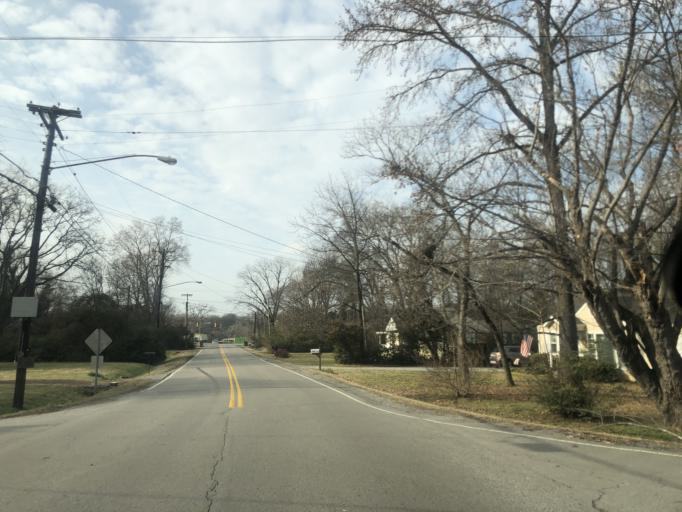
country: US
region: Tennessee
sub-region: Davidson County
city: Oak Hill
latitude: 36.1144
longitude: -86.7177
